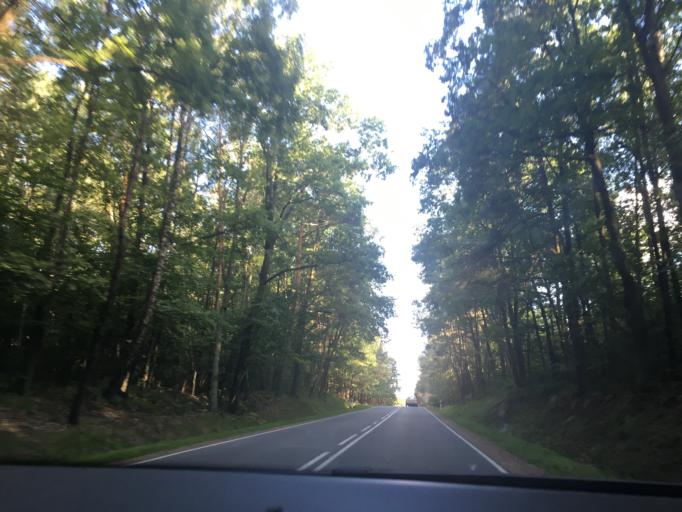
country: PL
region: Masovian Voivodeship
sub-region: Powiat losicki
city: Sarnaki
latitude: 52.3411
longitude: 22.8759
